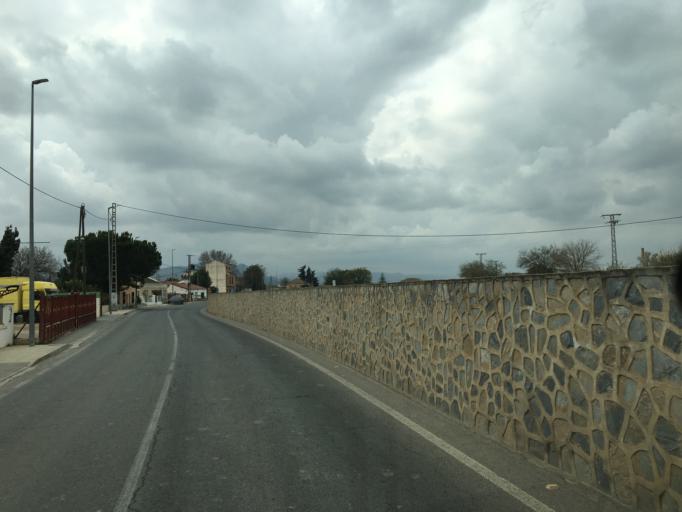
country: ES
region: Murcia
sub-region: Murcia
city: Beniel
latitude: 38.0366
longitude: -1.0127
